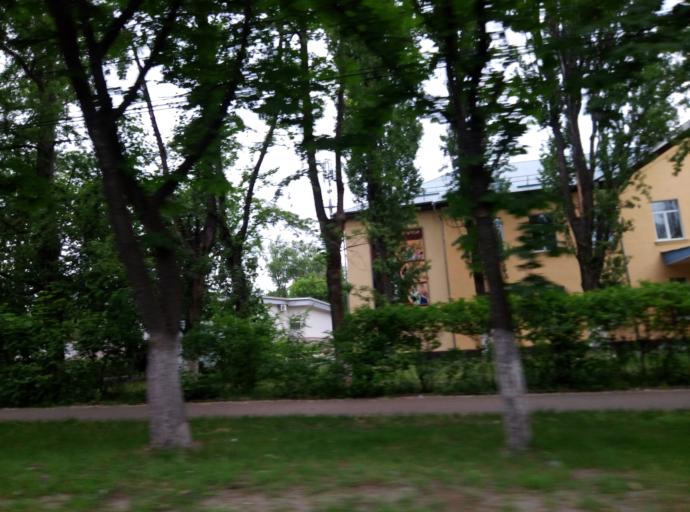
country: RU
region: Kursk
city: Kursk
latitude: 51.7094
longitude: 36.1494
